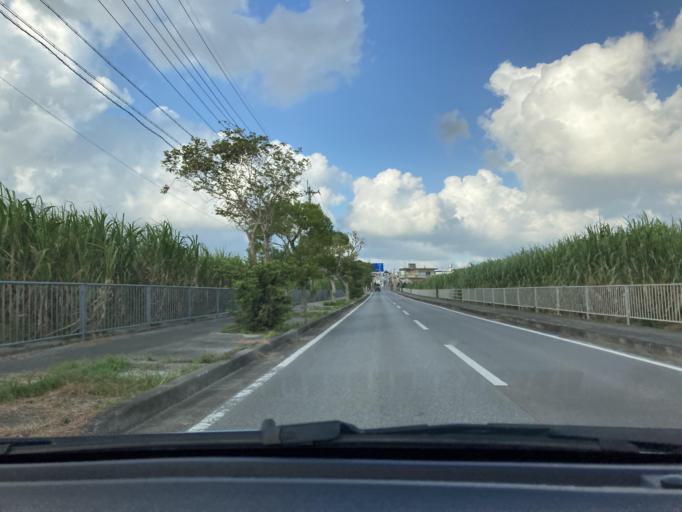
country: JP
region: Okinawa
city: Itoman
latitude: 26.1472
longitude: 127.7060
